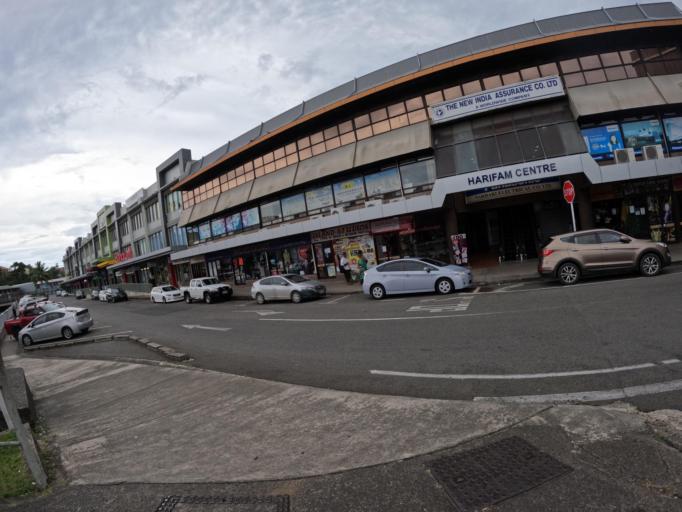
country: FJ
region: Central
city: Suva
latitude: -18.1388
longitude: 178.4263
